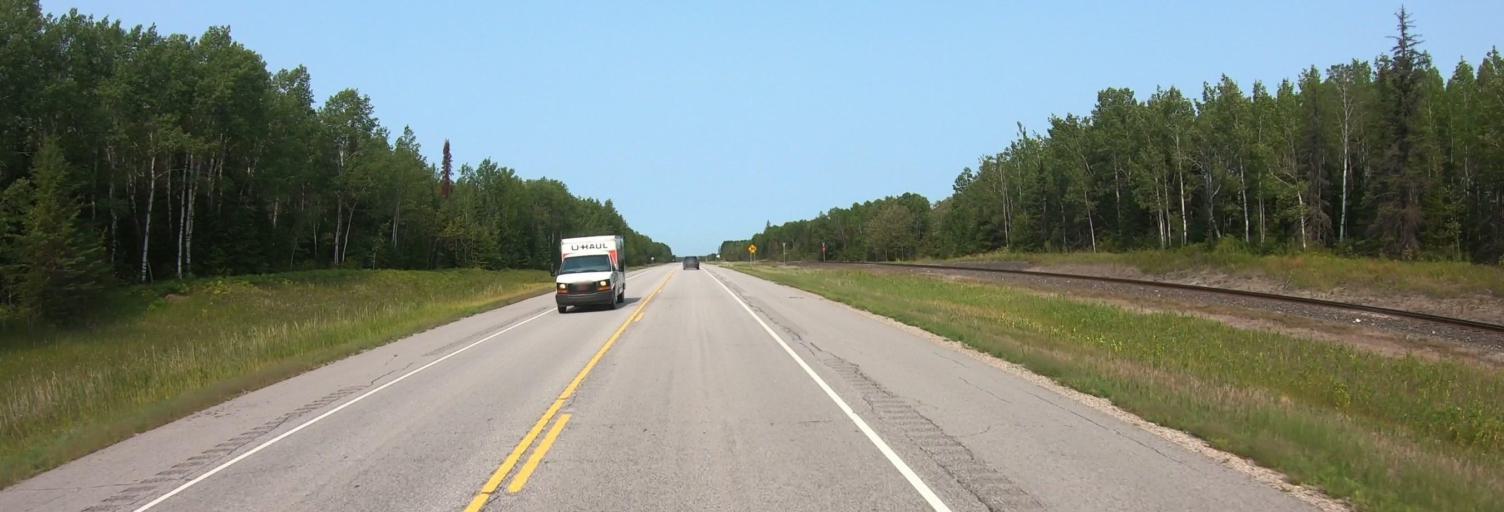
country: CA
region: Ontario
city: Fort Frances
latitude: 48.4613
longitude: -93.2870
